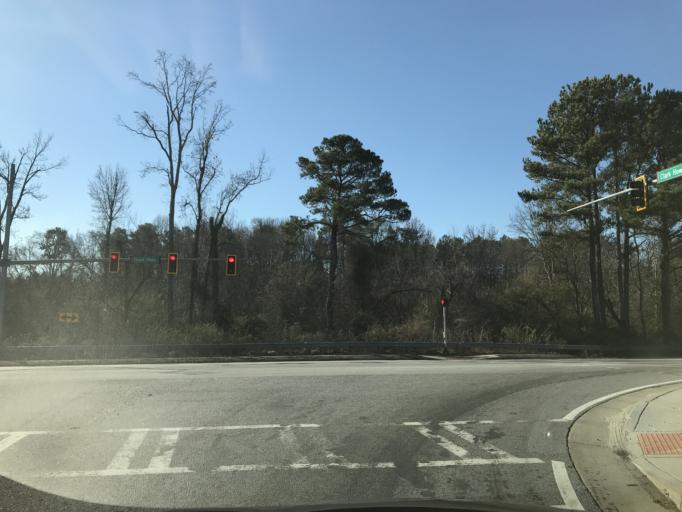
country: US
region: Georgia
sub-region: Clayton County
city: Forest Park
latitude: 33.6178
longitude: -84.4100
